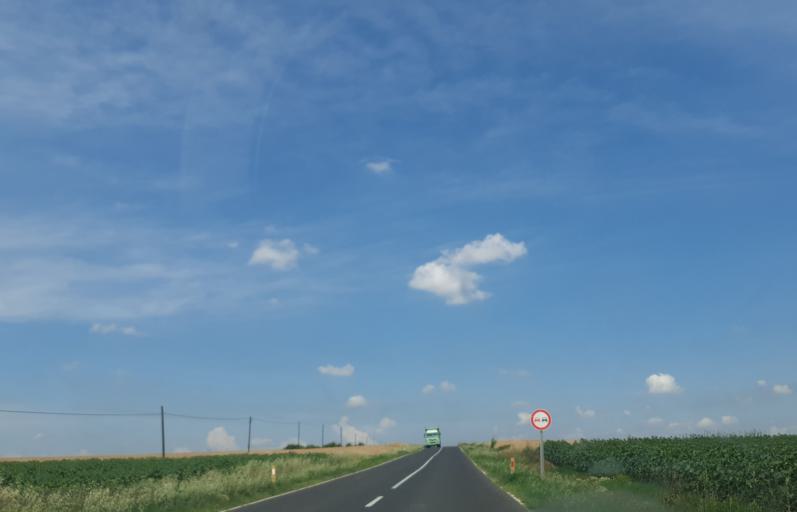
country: TR
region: Kirklareli
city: Buyukkaristiran
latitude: 41.2273
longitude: 27.5680
